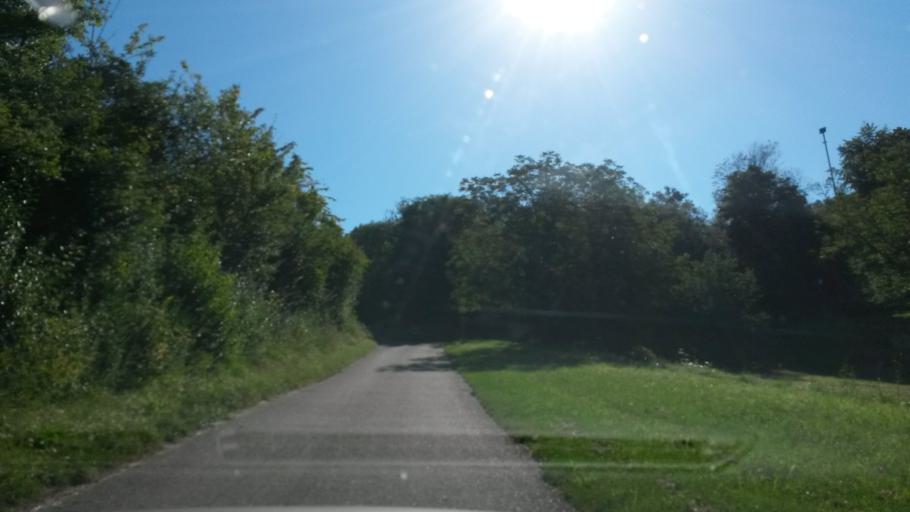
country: DE
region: Baden-Wuerttemberg
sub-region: Karlsruhe Region
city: Konigsbach-Stein
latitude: 48.9538
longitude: 8.6241
